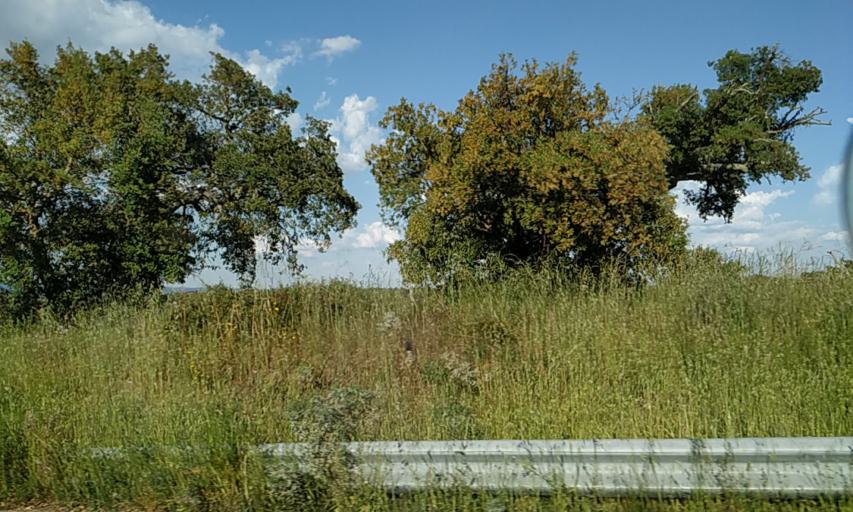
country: PT
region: Portalegre
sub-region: Portalegre
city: Urra
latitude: 39.1560
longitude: -7.4543
